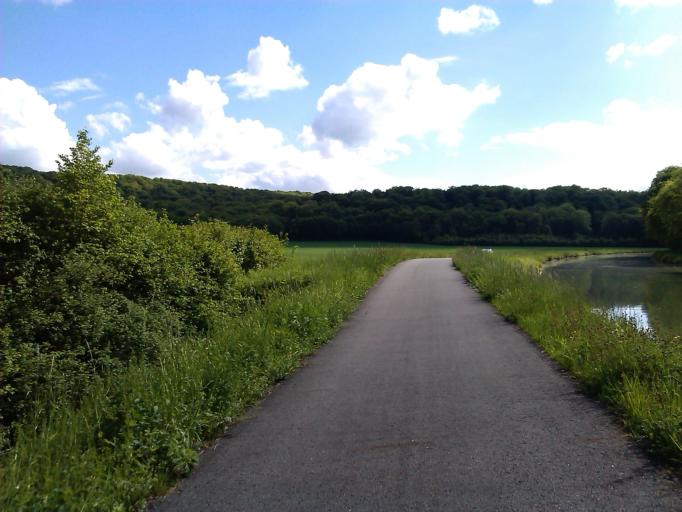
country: FR
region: Franche-Comte
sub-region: Departement du Doubs
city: Colombier-Fontaine
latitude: 47.4307
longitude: 6.6314
